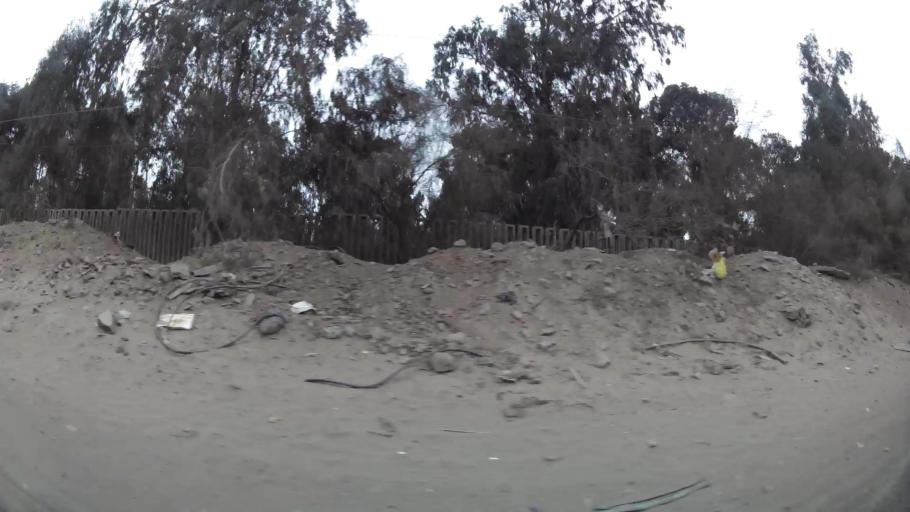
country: PE
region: Lima
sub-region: Lima
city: Surco
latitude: -12.1843
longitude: -76.9738
